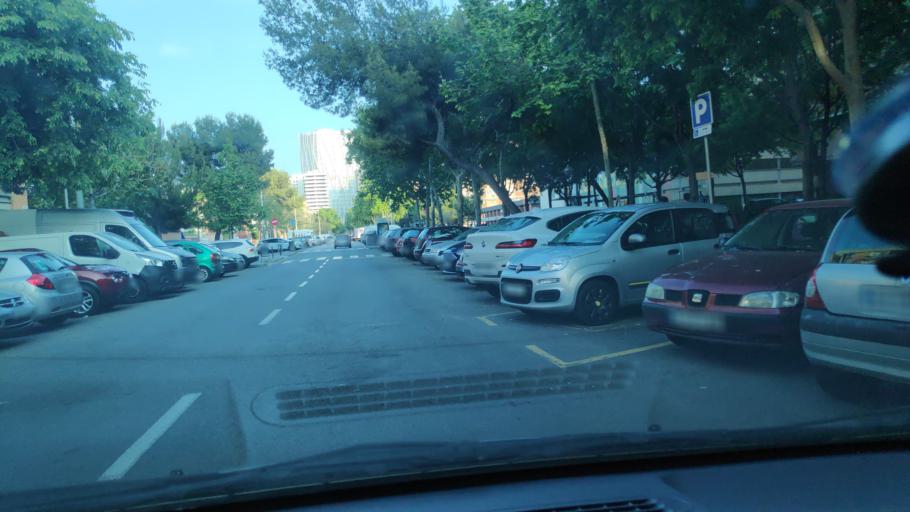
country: ES
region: Catalonia
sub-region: Provincia de Barcelona
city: Sant Adria de Besos
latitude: 41.4162
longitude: 2.2149
